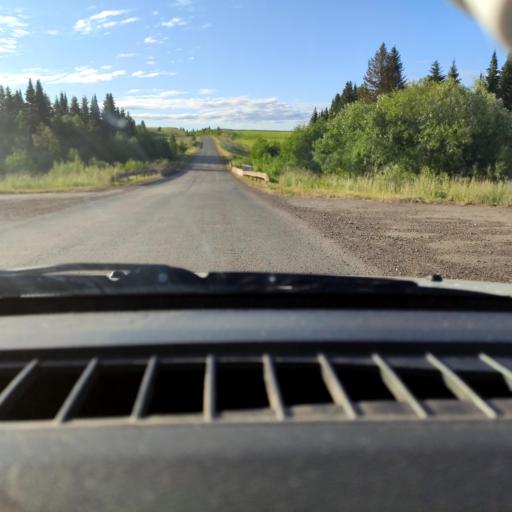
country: RU
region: Perm
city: Uinskoye
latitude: 57.0733
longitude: 56.5621
